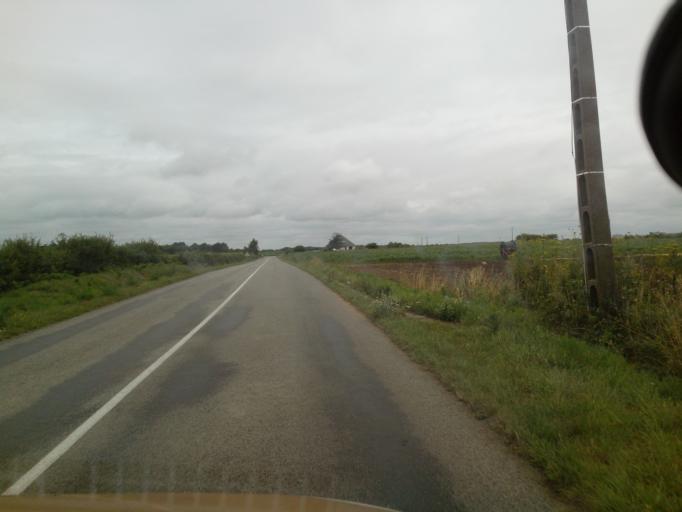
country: FR
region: Brittany
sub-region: Departement du Morbihan
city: Riantec
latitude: 47.6915
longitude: -3.2720
